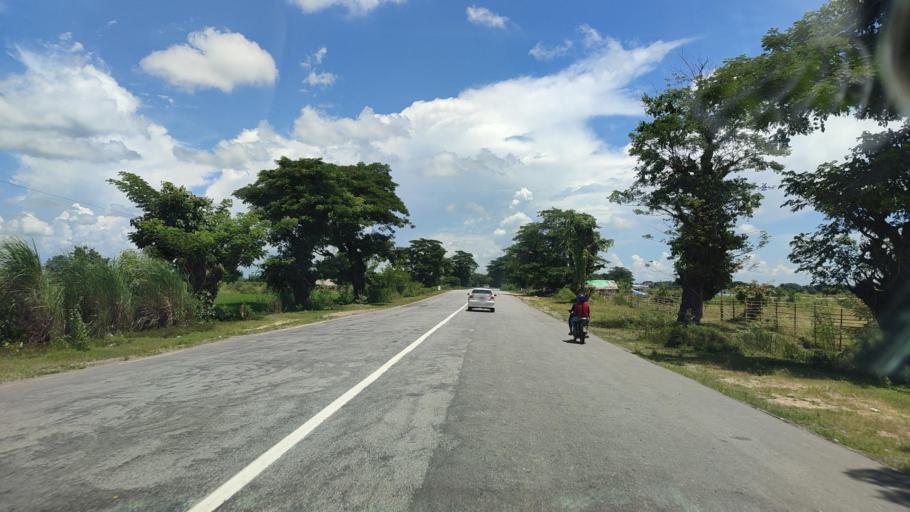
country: MM
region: Bago
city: Nyaunglebin
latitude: 18.1807
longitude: 96.5955
